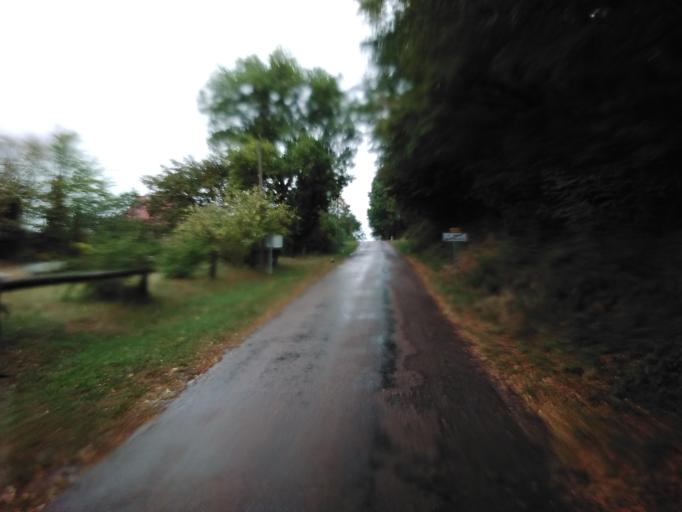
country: FR
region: Bourgogne
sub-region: Departement de la Nievre
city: Lormes
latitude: 47.3351
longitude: 3.9274
